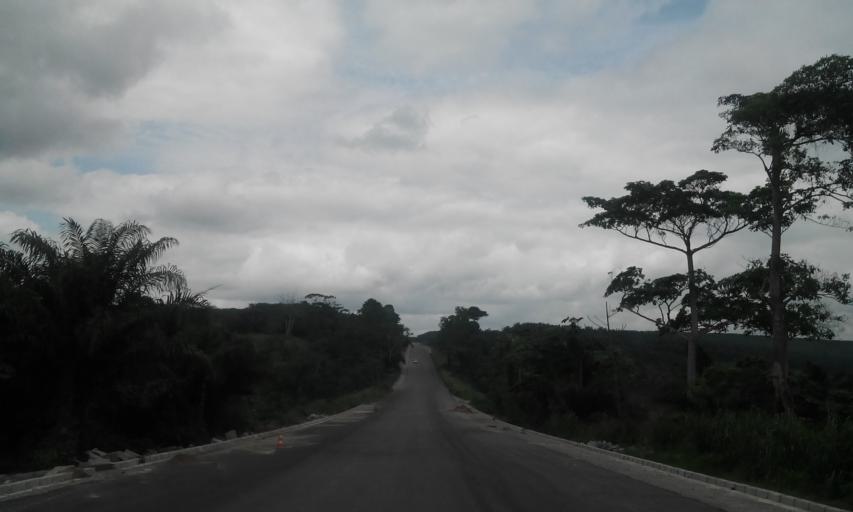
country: CI
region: Sud-Comoe
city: Mafere
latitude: 5.3105
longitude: -3.0470
